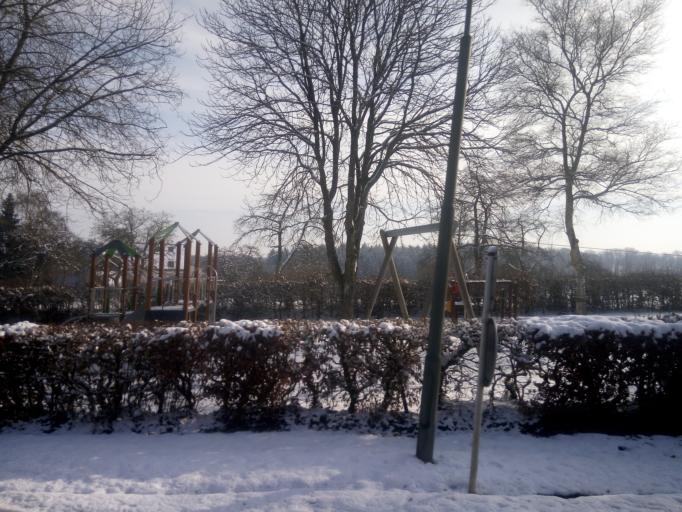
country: LU
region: Grevenmacher
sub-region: Canton d'Echternach
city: Consdorf
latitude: 49.7721
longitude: 6.3404
